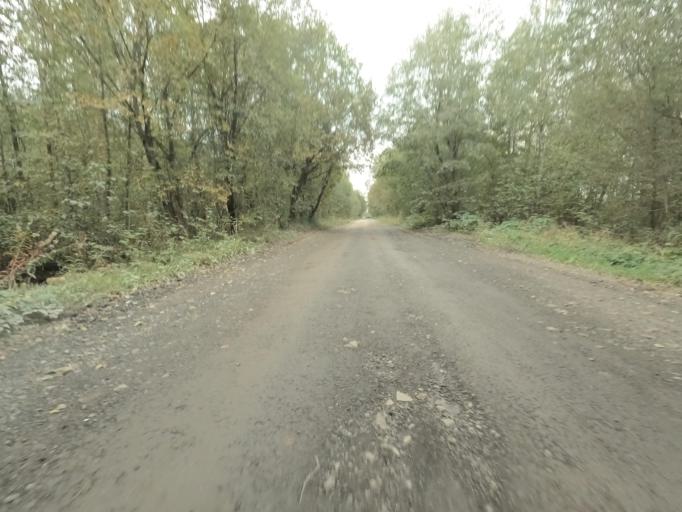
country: RU
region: St.-Petersburg
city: Sapernyy
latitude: 59.7616
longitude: 30.6512
